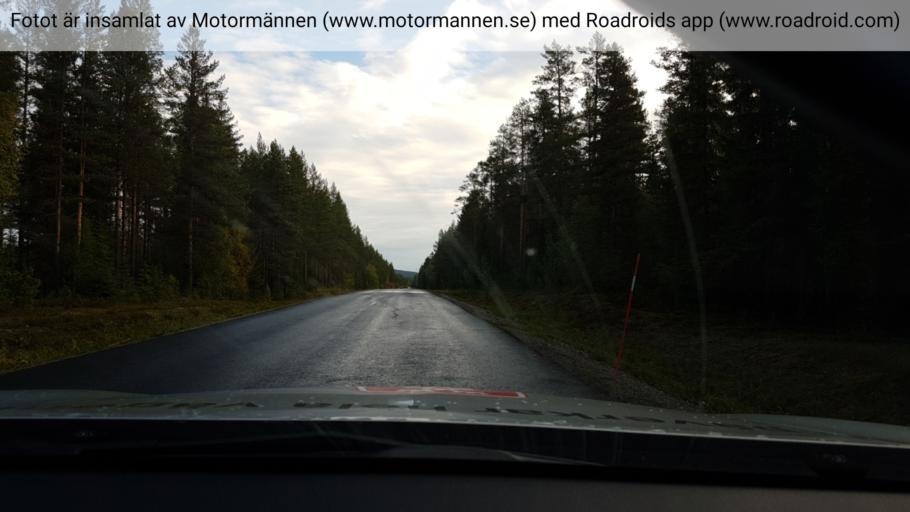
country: SE
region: Vaesterbotten
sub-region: Vindelns Kommun
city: Vindeln
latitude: 64.2272
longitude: 19.7748
